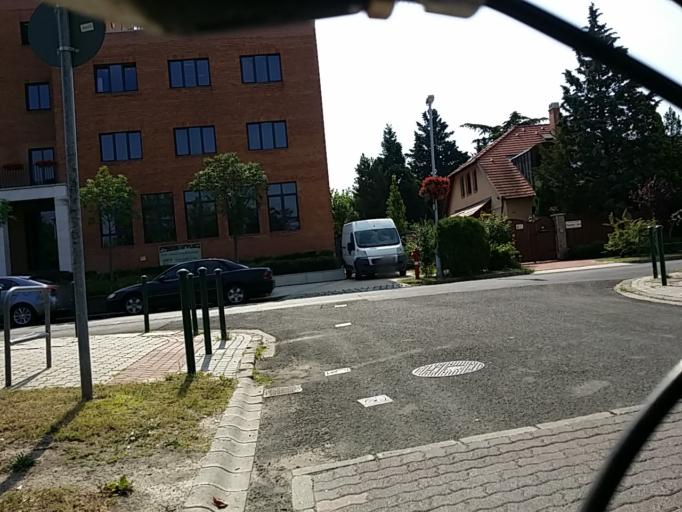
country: HU
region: Budapest
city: Budapest XIII. keruelet
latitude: 47.5461
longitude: 19.0832
